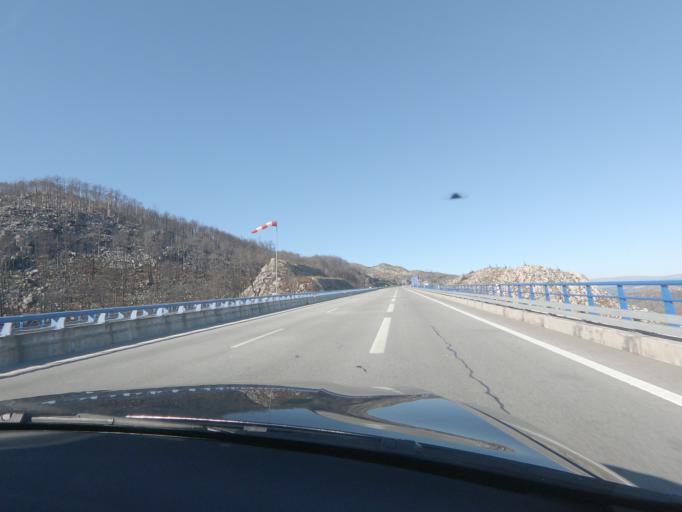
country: PT
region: Viseu
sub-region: Vouzela
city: Vouzela
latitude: 40.6701
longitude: -8.0754
